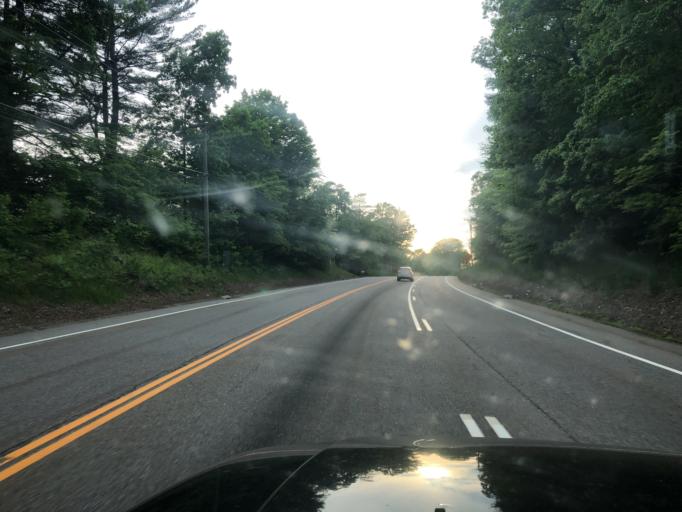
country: US
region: Connecticut
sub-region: Windham County
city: South Woodstock
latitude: 41.8770
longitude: -72.0880
